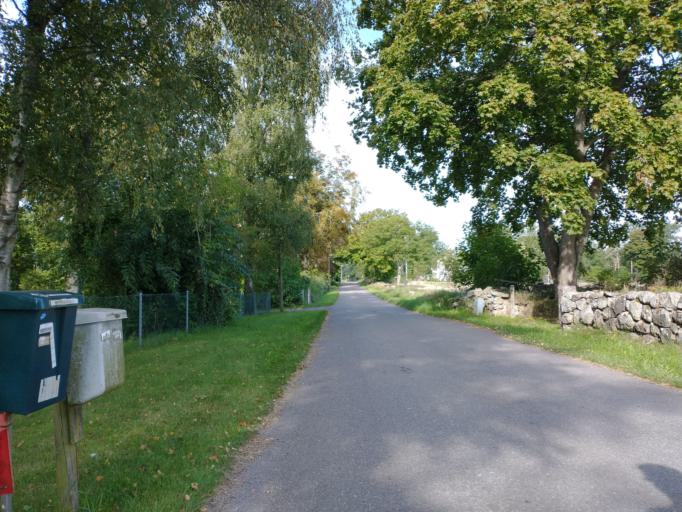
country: SE
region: Kalmar
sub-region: Kalmar Kommun
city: Lindsdal
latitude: 56.7780
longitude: 16.3083
